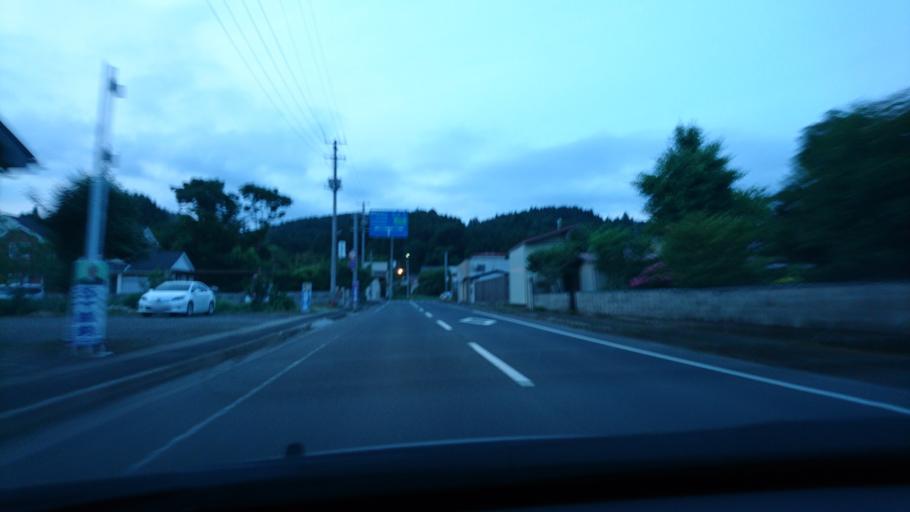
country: JP
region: Iwate
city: Ichinoseki
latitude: 38.8318
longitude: 140.9870
